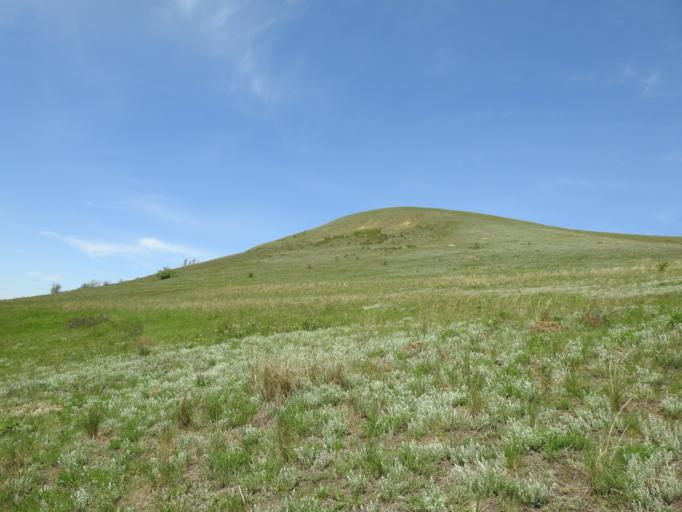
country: RU
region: Saratov
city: Krasnyy Oktyabr'
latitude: 51.5955
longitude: 45.7192
